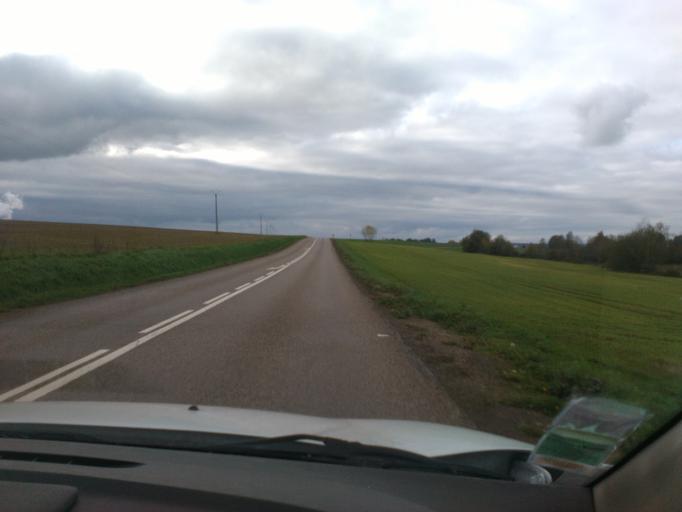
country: FR
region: Lorraine
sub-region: Departement des Vosges
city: Jeanmenil
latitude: 48.3467
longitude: 6.6740
